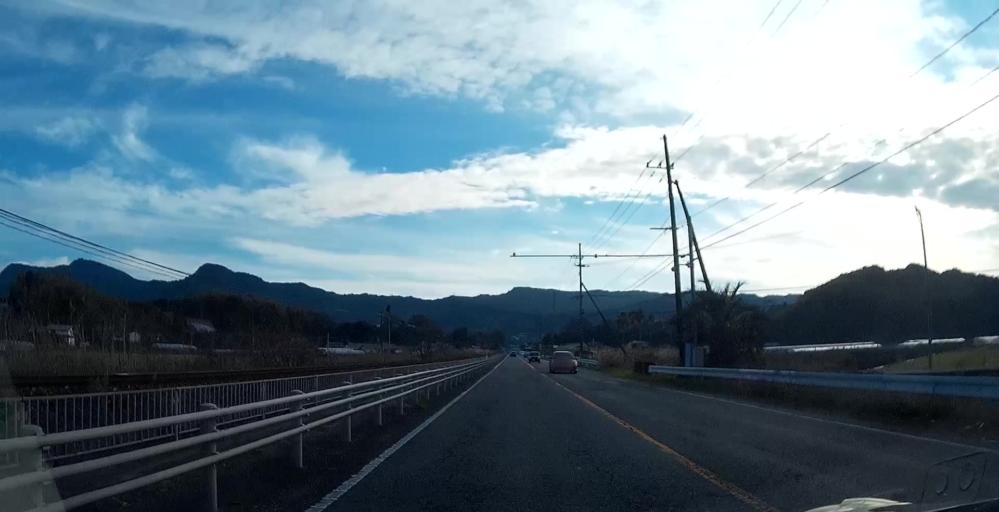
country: JP
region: Kumamoto
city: Uto
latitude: 32.6788
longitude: 130.5531
